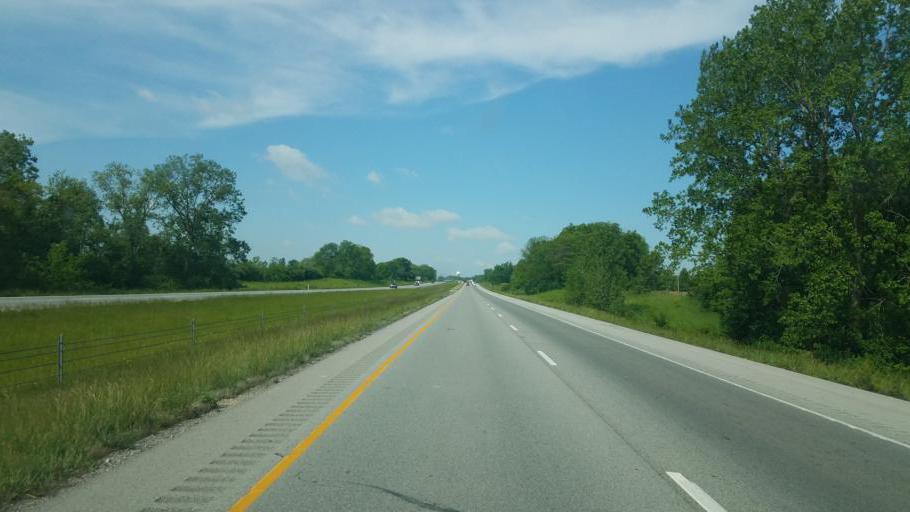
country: US
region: Indiana
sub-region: Morgan County
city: Mooresville
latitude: 39.6458
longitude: -86.4143
